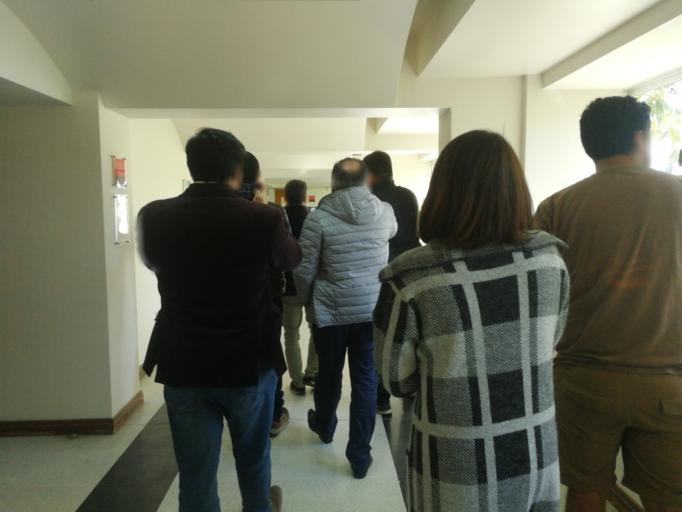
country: CL
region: Santiago Metropolitan
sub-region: Provincia de Santiago
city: Villa Presidente Frei, Nunoa, Santiago, Chile
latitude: -33.4069
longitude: -70.5520
